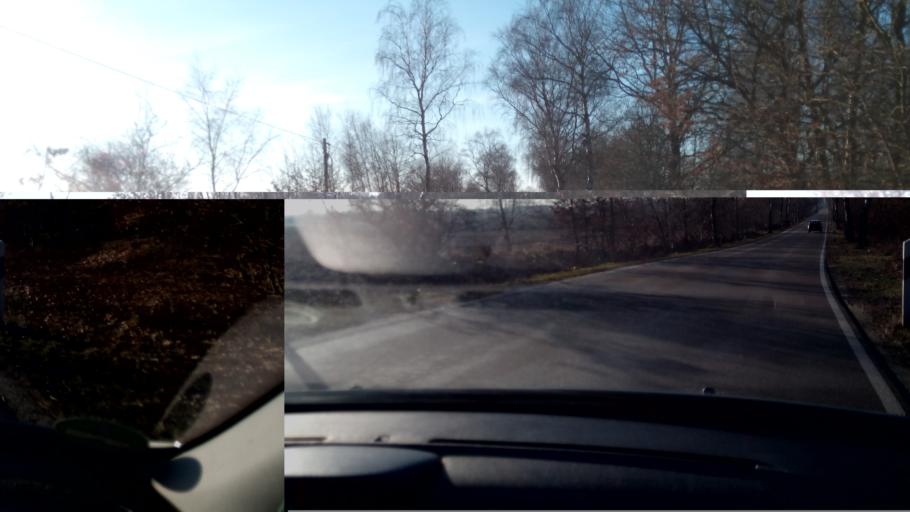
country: DE
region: Schleswig-Holstein
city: Fitzen
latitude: 53.4872
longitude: 10.6562
